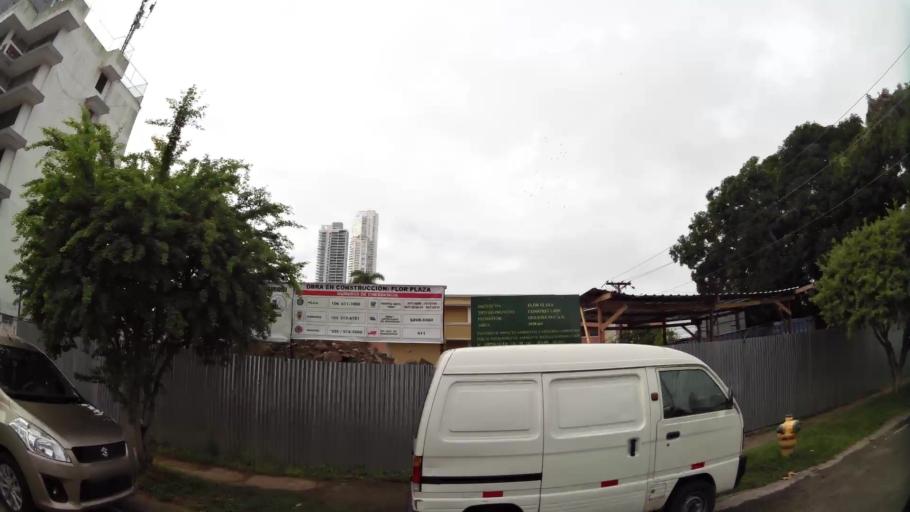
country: PA
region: Panama
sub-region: Distrito de Panama
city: Ancon
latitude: 8.9721
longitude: -79.5318
